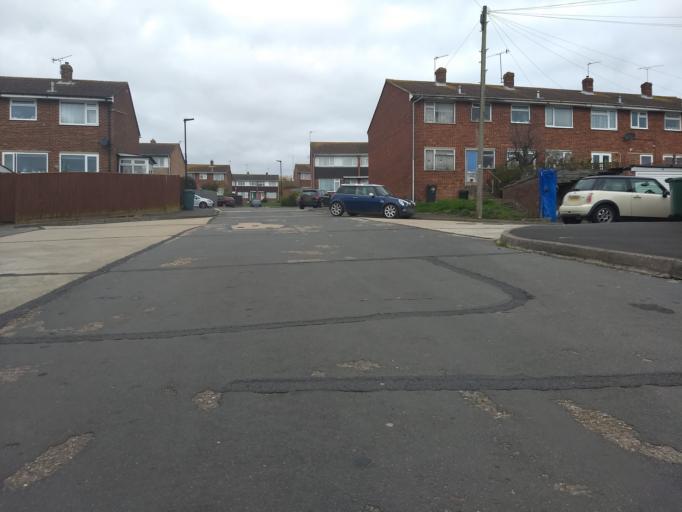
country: GB
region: England
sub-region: Isle of Wight
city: Ryde
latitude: 50.7231
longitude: -1.1618
